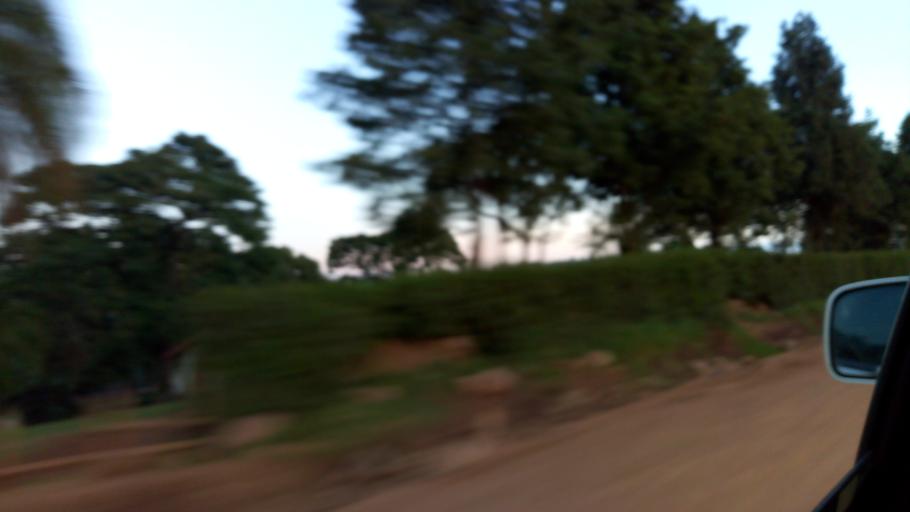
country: KE
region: Nyamira District
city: Nyamira
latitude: -0.5851
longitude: 35.0515
